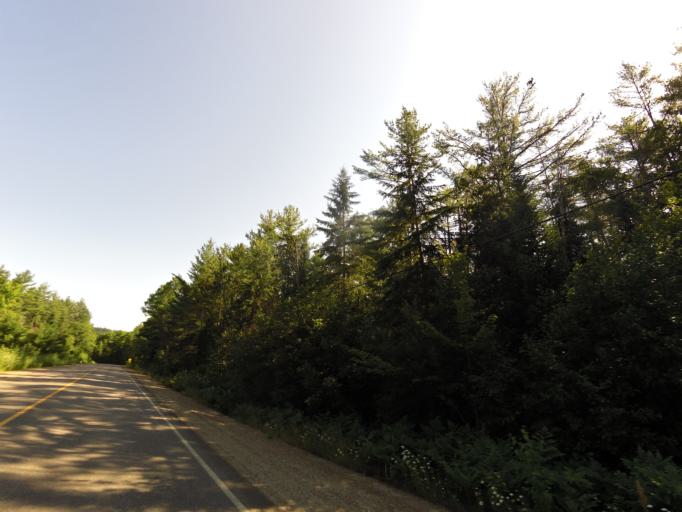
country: CA
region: Ontario
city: Deep River
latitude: 46.1881
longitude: -77.6809
